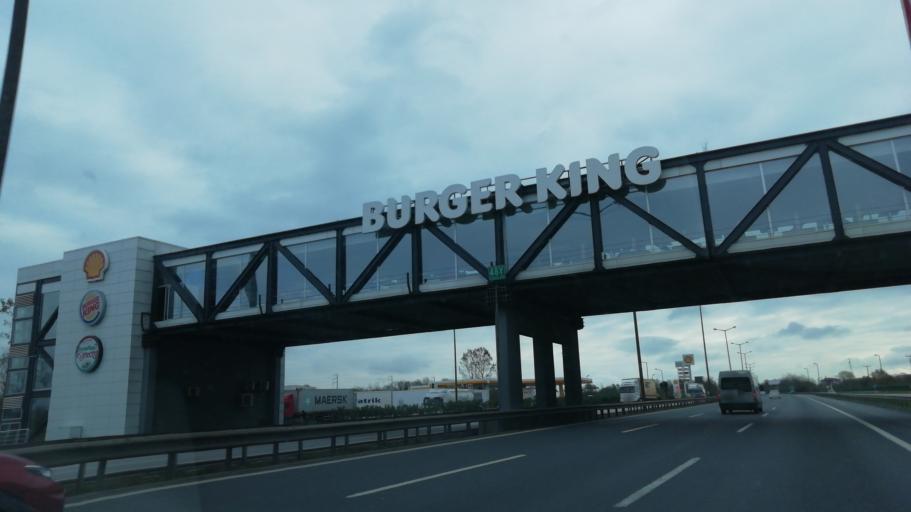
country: TR
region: Kocaeli
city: Derbent
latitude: 40.7276
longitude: 30.0695
